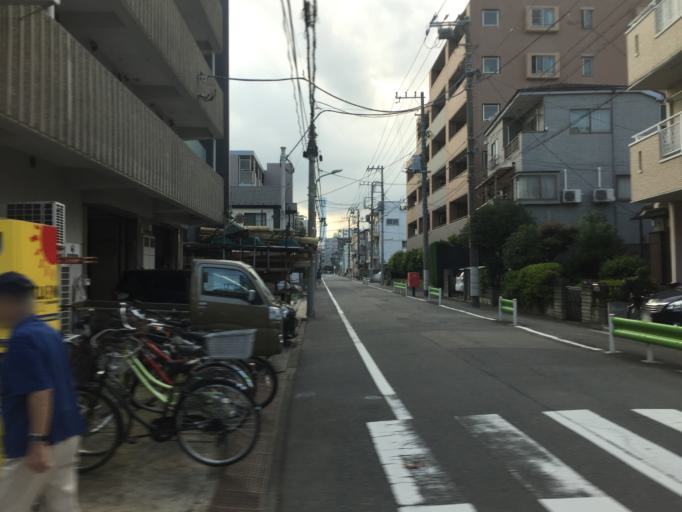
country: JP
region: Kanagawa
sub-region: Kawasaki-shi
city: Kawasaki
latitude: 35.5617
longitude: 139.6955
